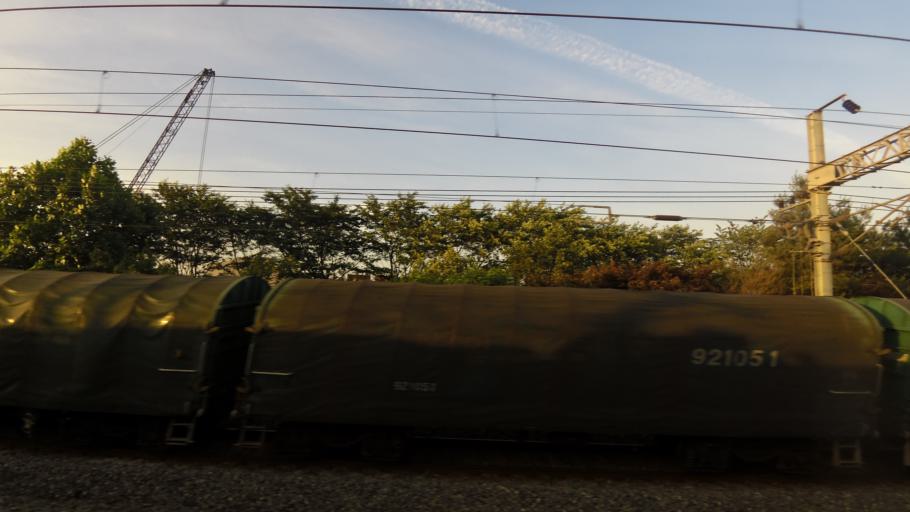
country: KR
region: Gyeonggi-do
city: Osan
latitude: 37.0380
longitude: 127.0670
